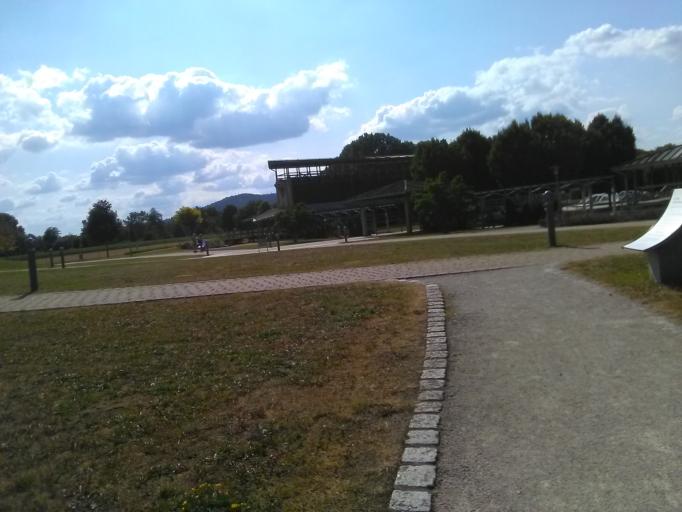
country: DE
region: Bavaria
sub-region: Upper Franconia
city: Bad Staffelstein
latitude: 50.1098
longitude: 10.9888
